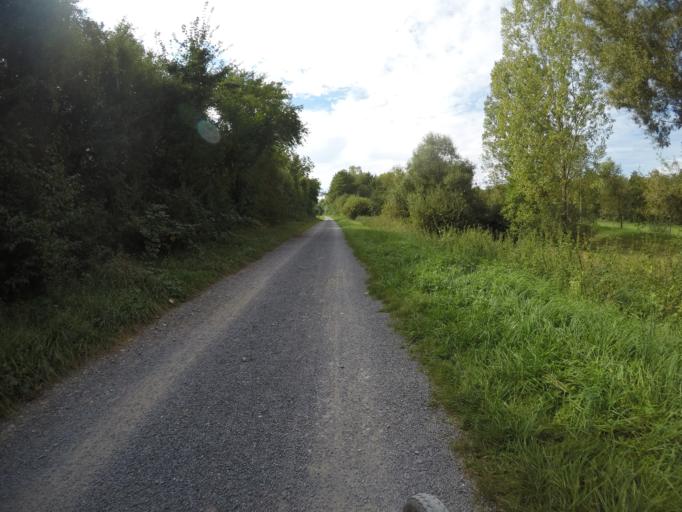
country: DE
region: Baden-Wuerttemberg
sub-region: Karlsruhe Region
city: Ubstadt-Weiher
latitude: 49.1723
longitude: 8.6356
